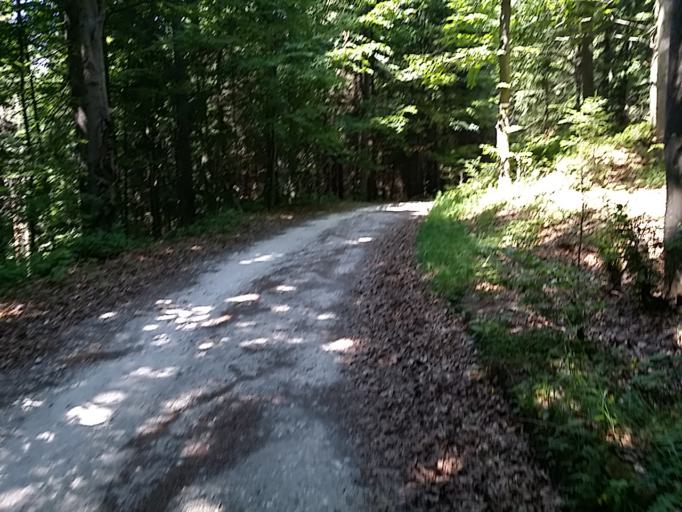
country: SK
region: Kosicky
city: Dobsina
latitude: 48.9210
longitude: 20.3825
